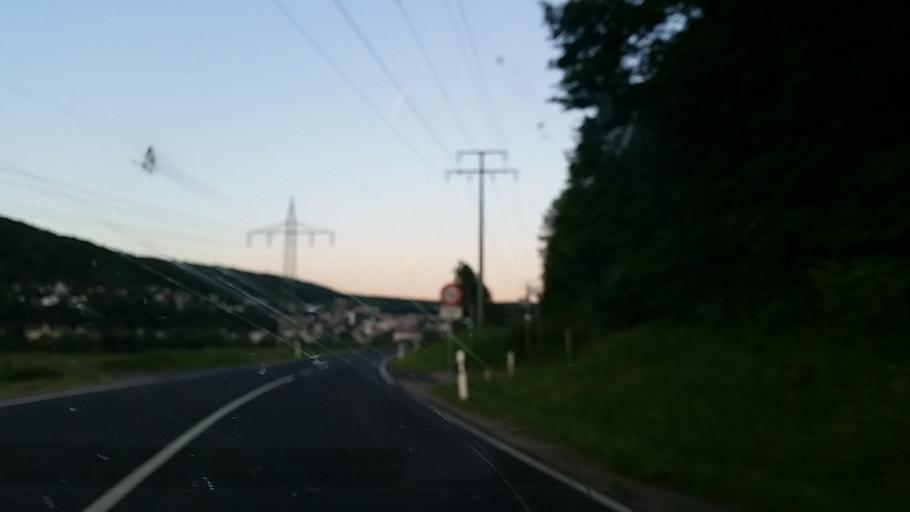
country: DE
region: Bavaria
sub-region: Regierungsbezirk Unterfranken
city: Gemunden
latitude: 50.0528
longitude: 9.6852
